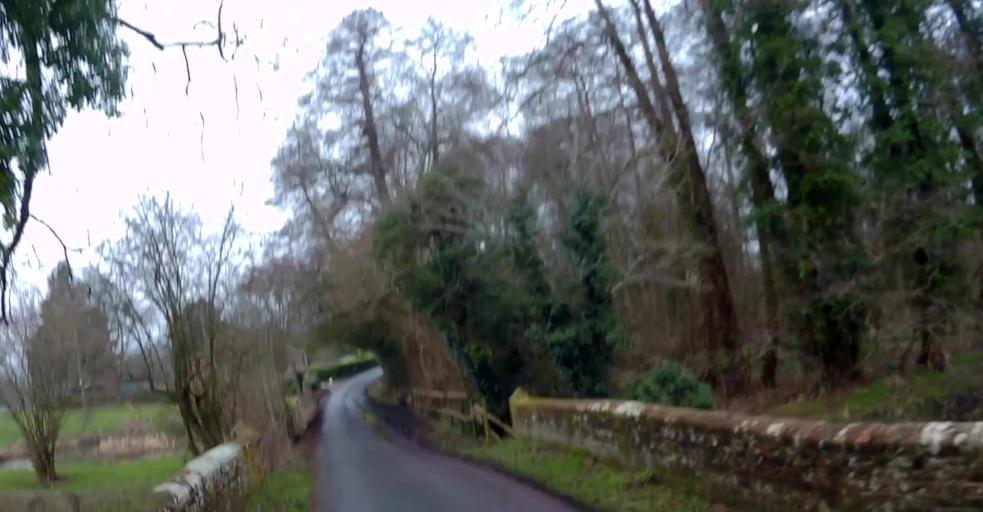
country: GB
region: England
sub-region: Hampshire
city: Eversley
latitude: 51.3332
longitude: -0.9271
